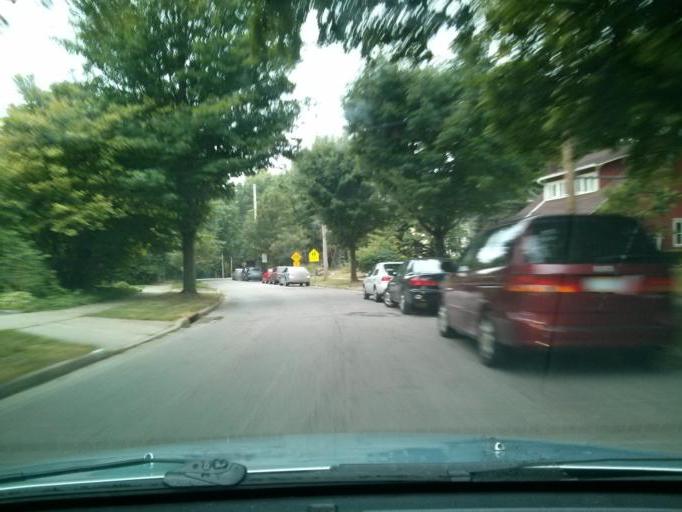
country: US
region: Ohio
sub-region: Portage County
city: Kent
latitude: 41.1564
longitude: -81.3656
